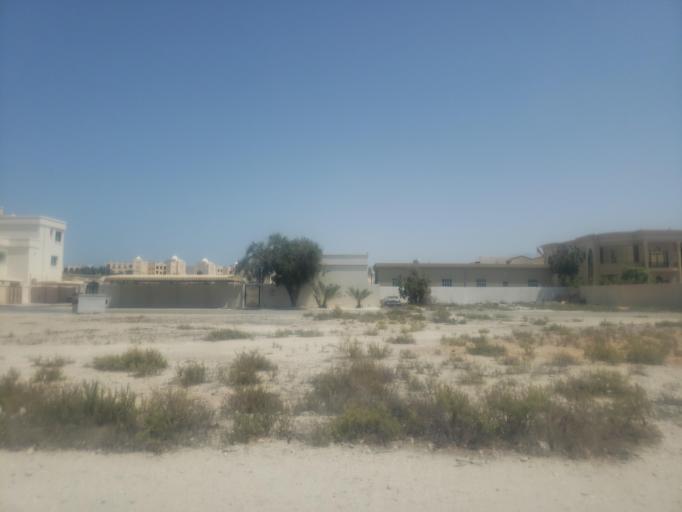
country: AE
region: Ra's al Khaymah
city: Ras al-Khaimah
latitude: 25.8097
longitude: 55.9563
